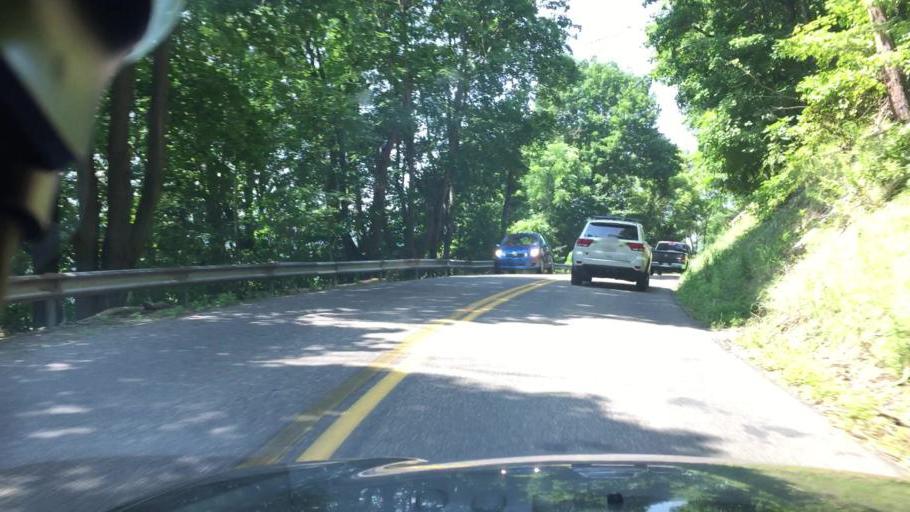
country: US
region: Pennsylvania
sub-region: Columbia County
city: Catawissa
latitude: 40.9519
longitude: -76.4512
